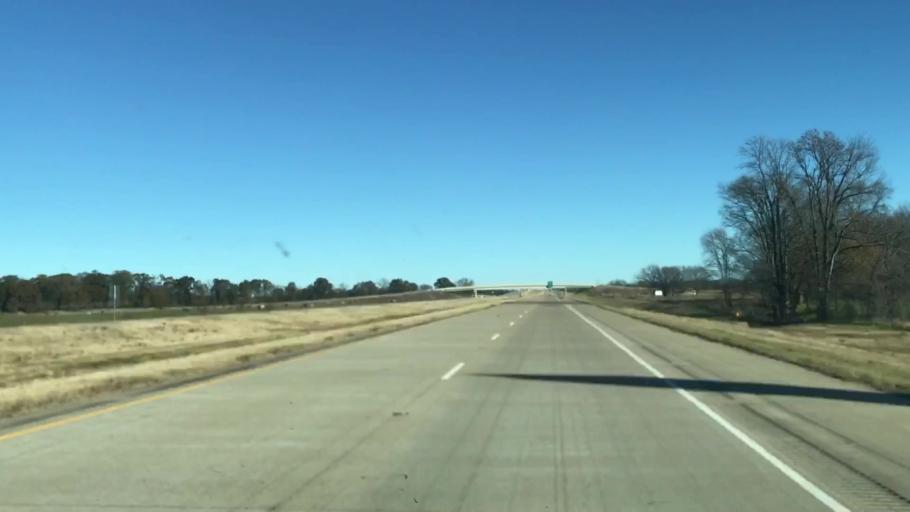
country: US
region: Louisiana
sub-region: Caddo Parish
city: Vivian
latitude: 32.8401
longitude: -93.8700
